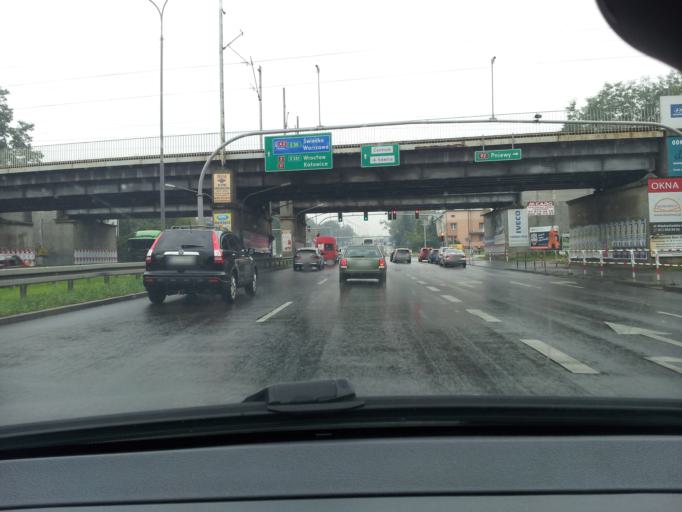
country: PL
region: Greater Poland Voivodeship
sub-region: Poznan
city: Poznan
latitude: 52.4210
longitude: 16.8943
